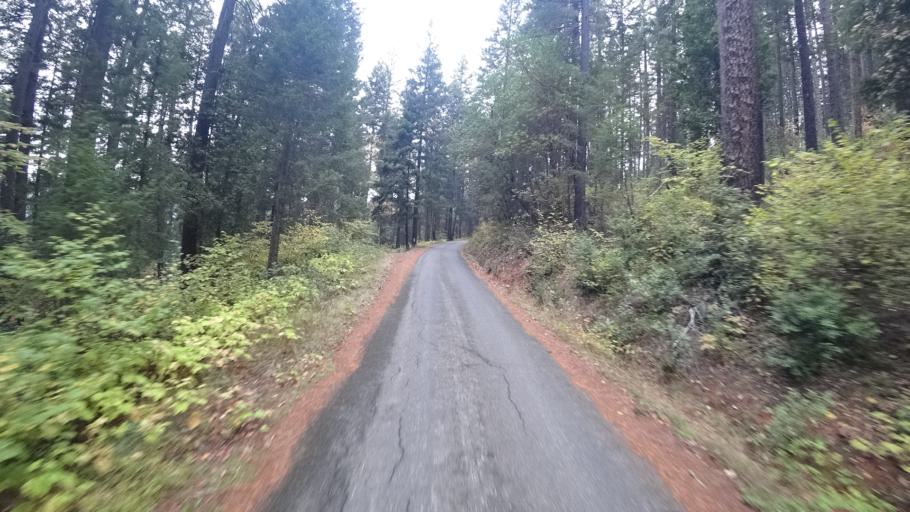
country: US
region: California
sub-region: Siskiyou County
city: Happy Camp
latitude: 41.8049
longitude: -123.3394
